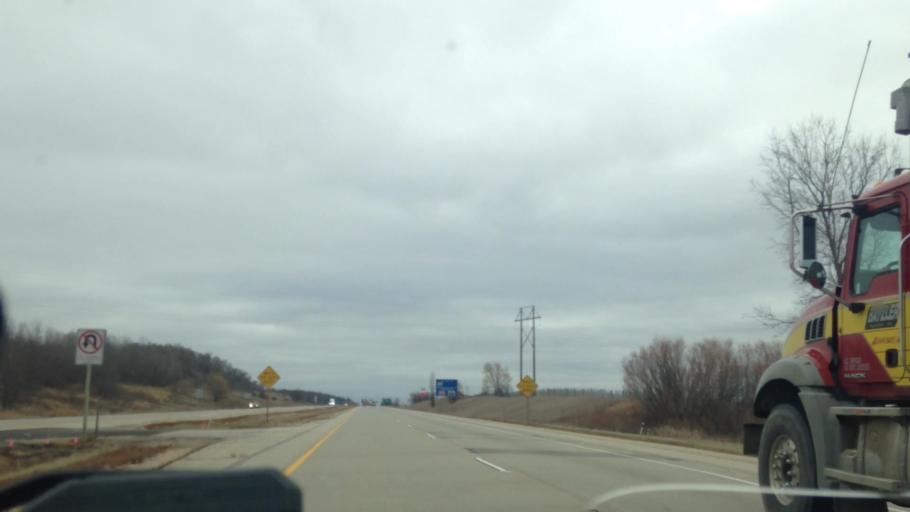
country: US
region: Wisconsin
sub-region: Washington County
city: Slinger
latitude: 43.3801
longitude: -88.3052
